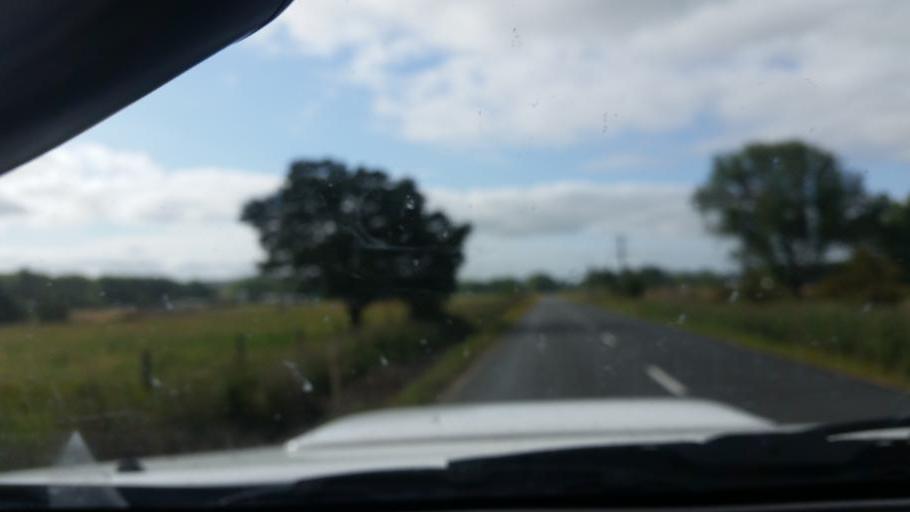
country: NZ
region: Northland
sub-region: Kaipara District
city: Dargaville
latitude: -35.8328
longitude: 173.8420
